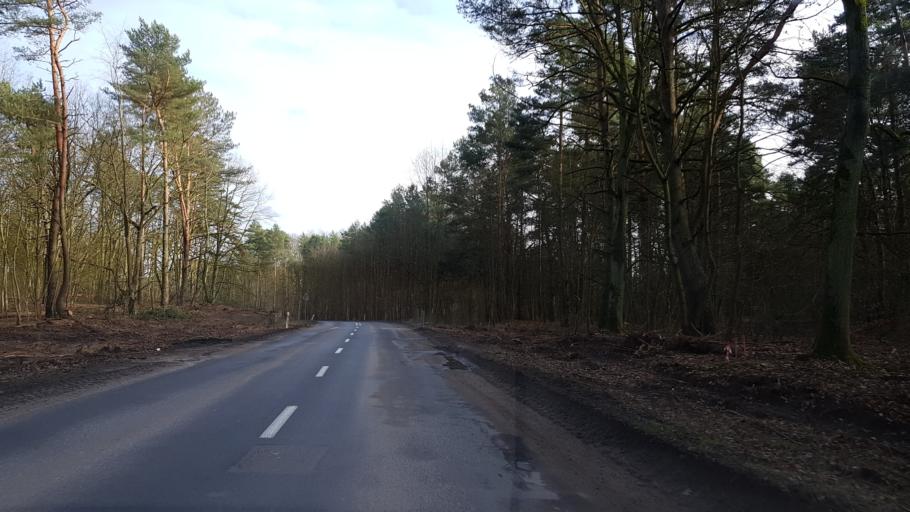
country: PL
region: West Pomeranian Voivodeship
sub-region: Szczecin
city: Szczecin
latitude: 53.4726
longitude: 14.4751
